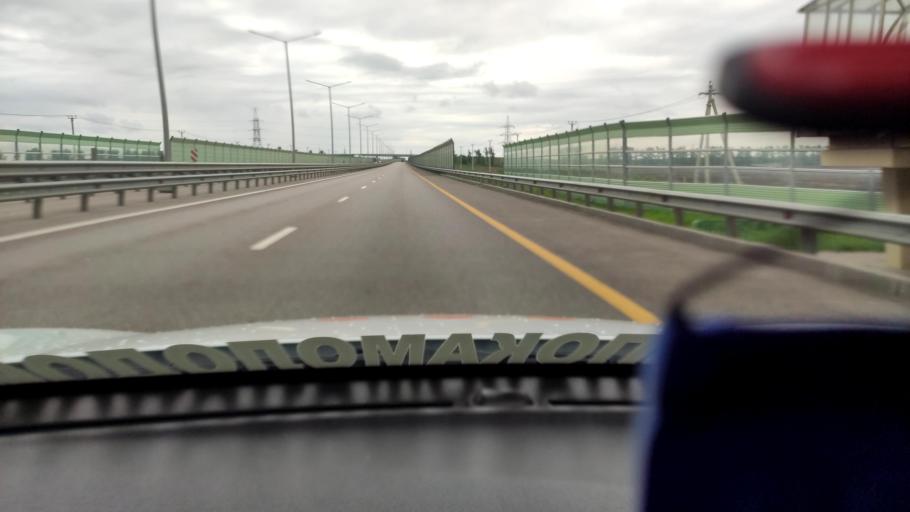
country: RU
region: Voronezj
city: Novaya Usman'
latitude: 51.6209
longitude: 39.3183
